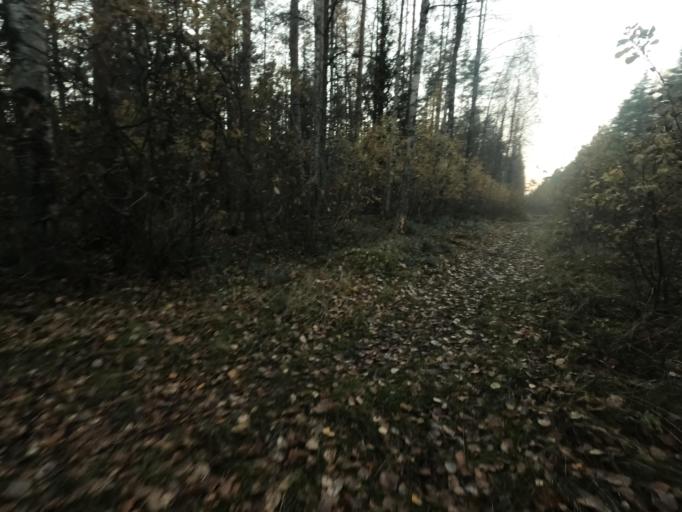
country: RU
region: St.-Petersburg
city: Komarovo
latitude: 60.2011
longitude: 29.8120
